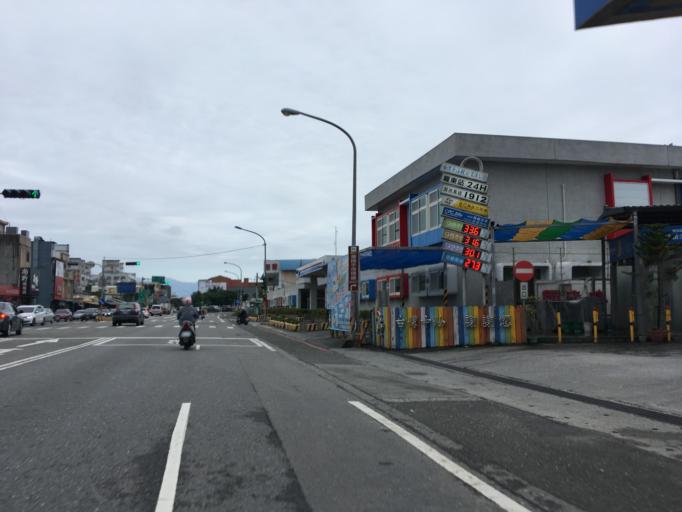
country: TW
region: Taiwan
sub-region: Yilan
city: Yilan
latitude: 24.6976
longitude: 121.7691
